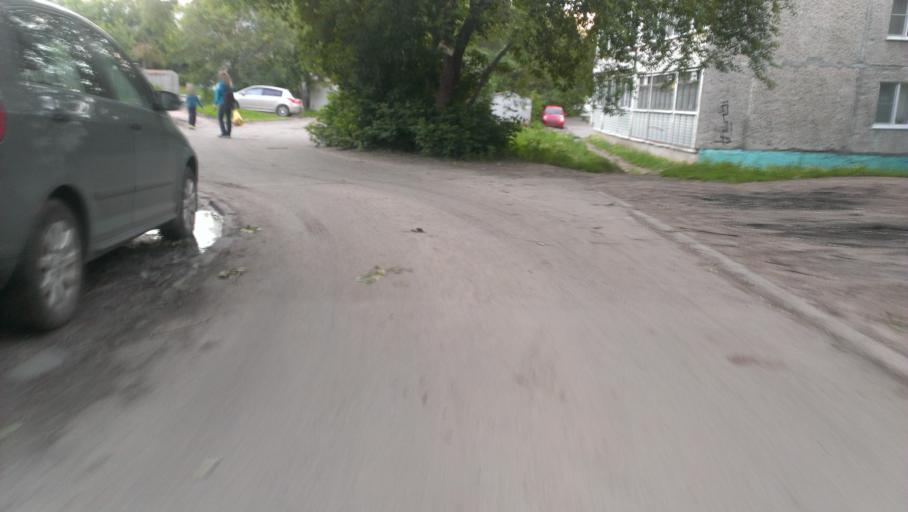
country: RU
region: Altai Krai
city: Novosilikatnyy
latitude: 53.3763
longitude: 83.6781
